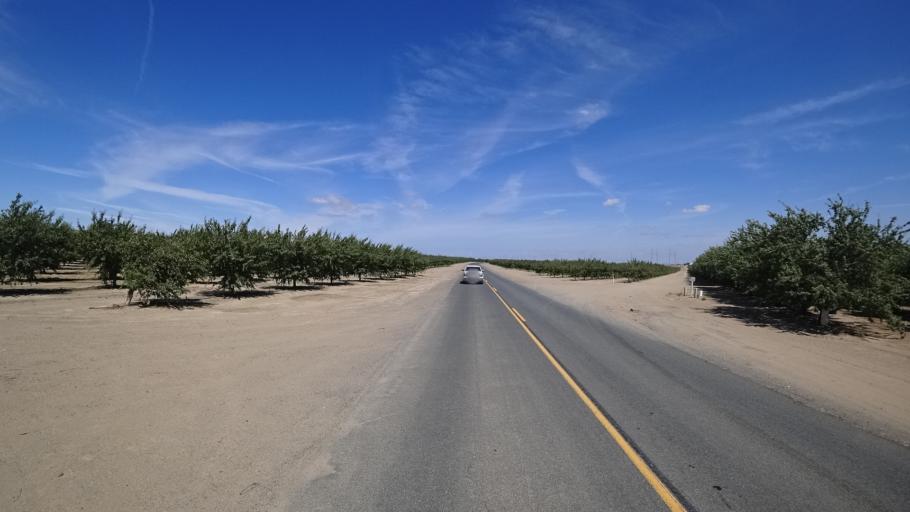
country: US
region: California
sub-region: Kings County
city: Kettleman City
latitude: 35.9813
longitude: -119.9501
